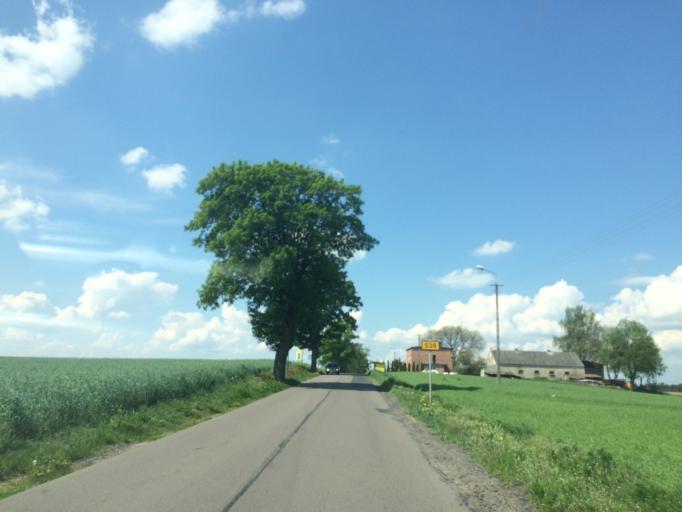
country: PL
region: Warmian-Masurian Voivodeship
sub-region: Powiat ilawski
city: Lubawa
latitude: 53.4353
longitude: 19.7128
